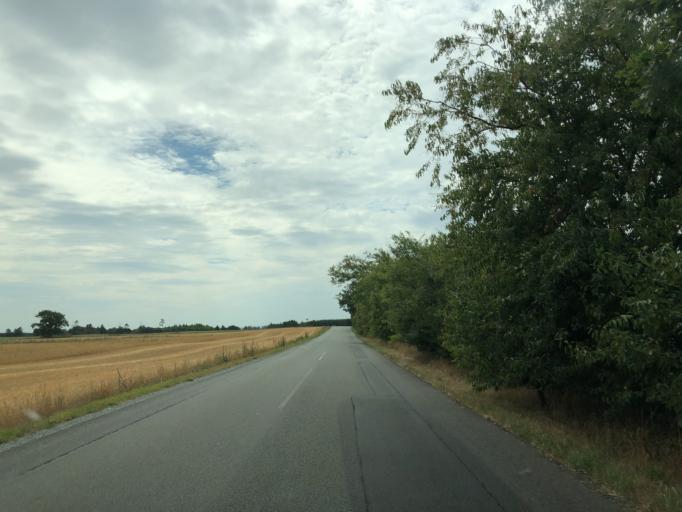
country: DK
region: South Denmark
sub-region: Vejle Kommune
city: Egtved
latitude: 55.6230
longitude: 9.1934
